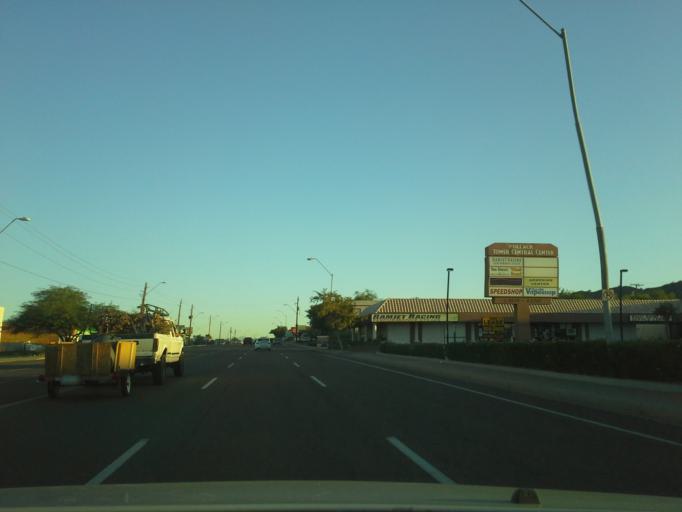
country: US
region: Arizona
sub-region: Maricopa County
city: Paradise Valley
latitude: 33.6058
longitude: -112.0365
